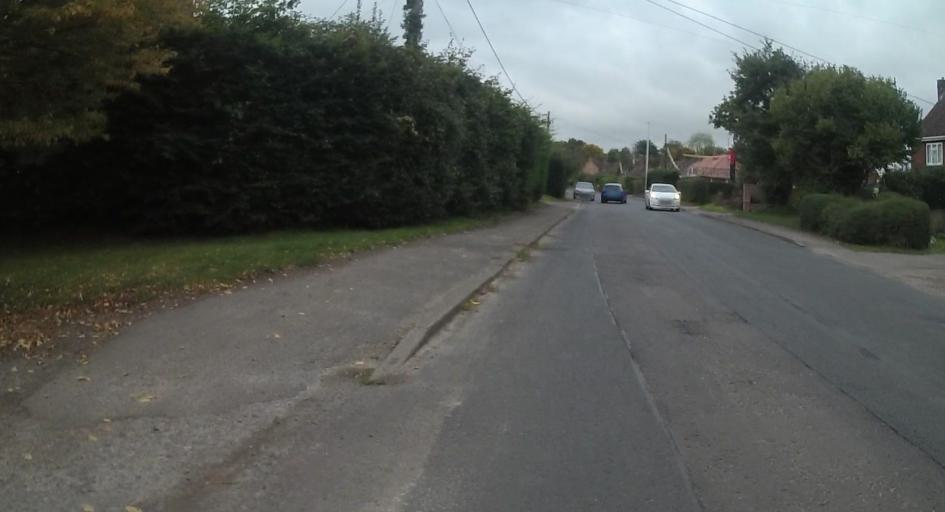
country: GB
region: England
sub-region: Hampshire
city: Fleet
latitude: 51.2696
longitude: -0.8646
